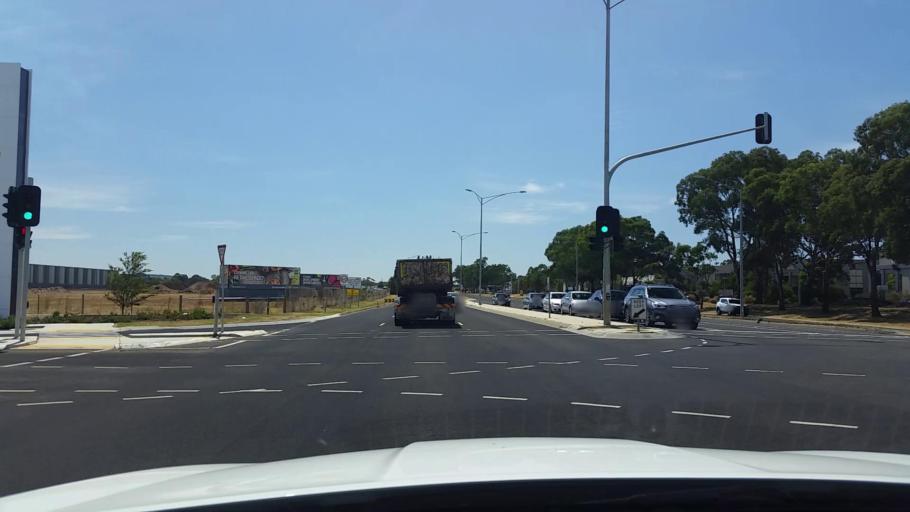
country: AU
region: Victoria
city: Heatherton
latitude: -37.9787
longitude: 145.1106
